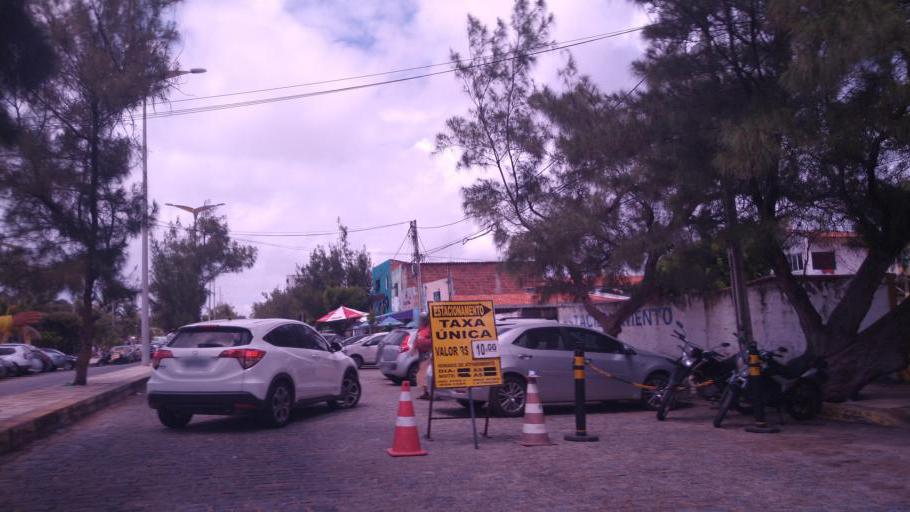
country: BR
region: Ceara
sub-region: Fortaleza
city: Fortaleza
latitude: -3.7332
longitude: -38.4567
